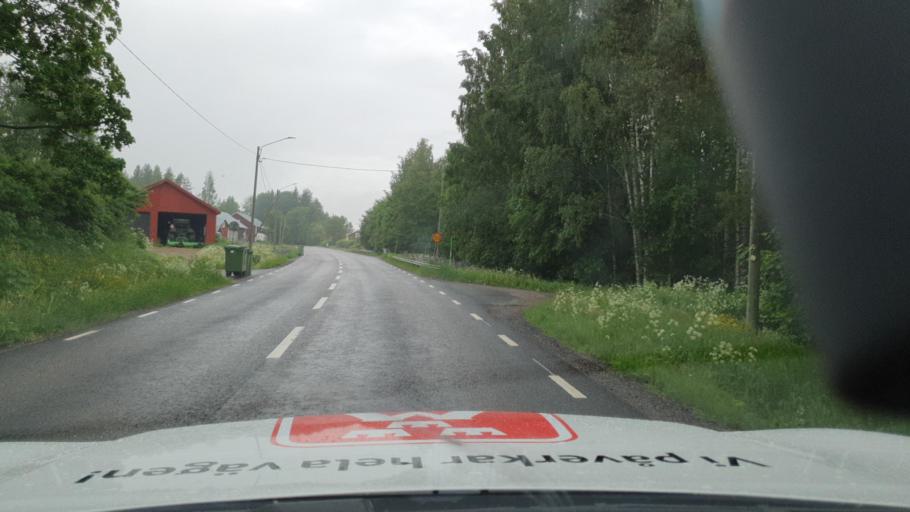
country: SE
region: Vaesterbotten
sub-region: Vannas Kommun
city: Vaennaes
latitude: 63.7833
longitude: 19.8401
